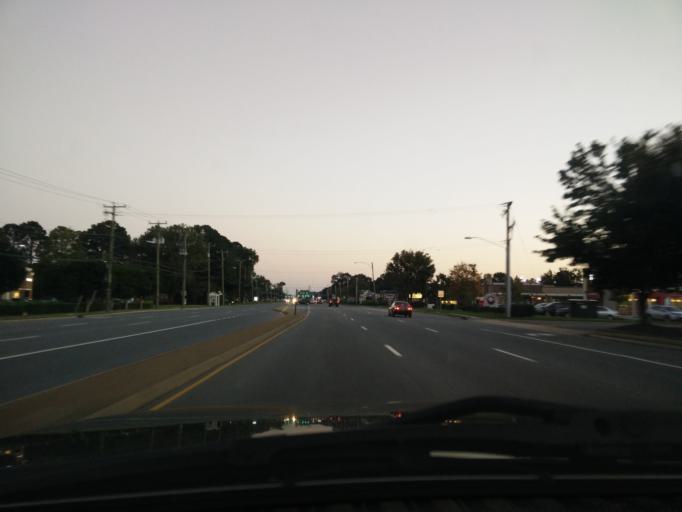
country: US
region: Virginia
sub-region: City of Chesapeake
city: Chesapeake
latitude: 36.7635
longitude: -76.2514
